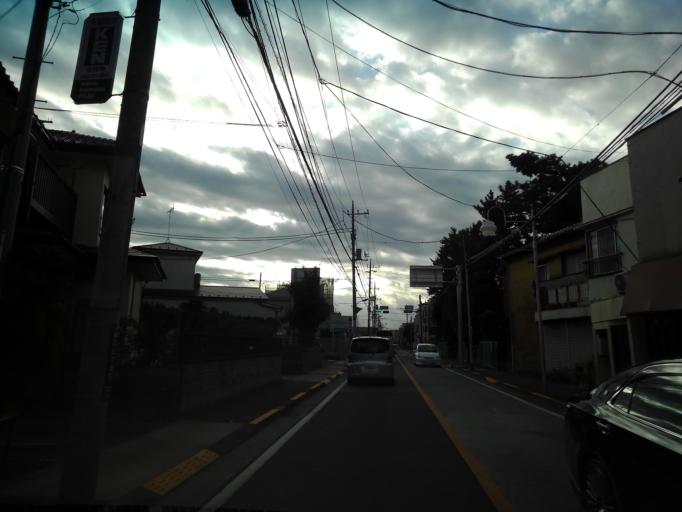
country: JP
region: Tokyo
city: Mitaka-shi
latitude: 35.6805
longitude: 139.5708
